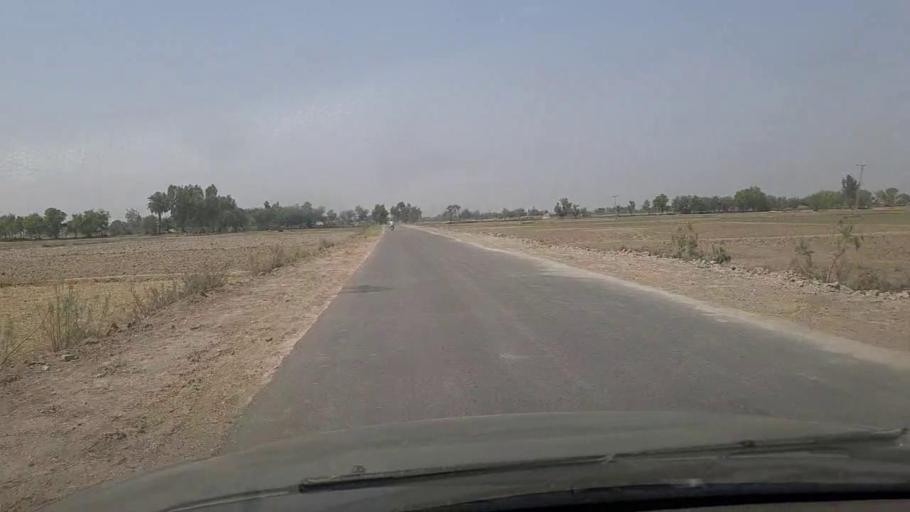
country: PK
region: Sindh
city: Khanpur
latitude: 27.8771
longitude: 69.4612
